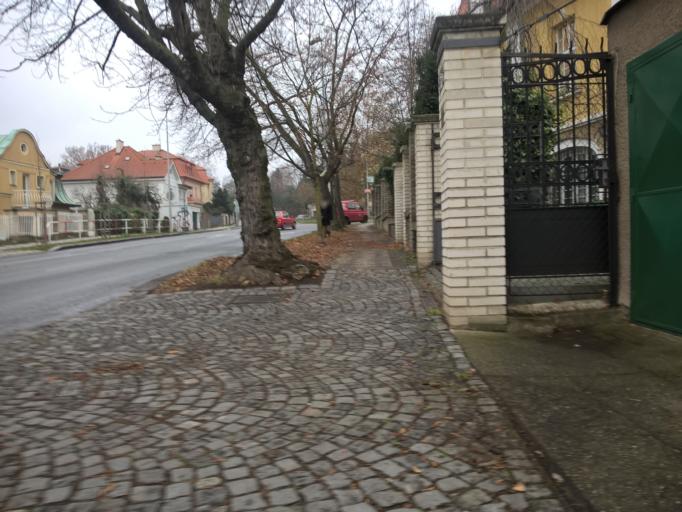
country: CZ
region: Praha
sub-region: Praha 1
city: Mala Strana
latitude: 50.0752
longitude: 14.3898
